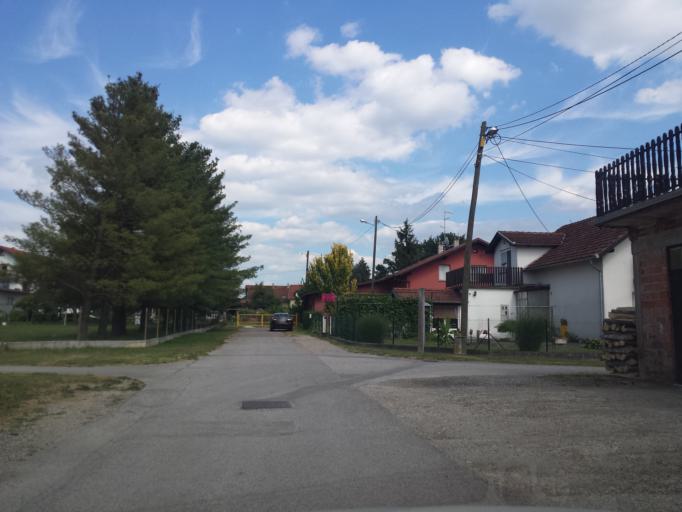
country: HR
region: Grad Zagreb
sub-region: Sesvete
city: Sesvete
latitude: 45.8219
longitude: 16.1559
